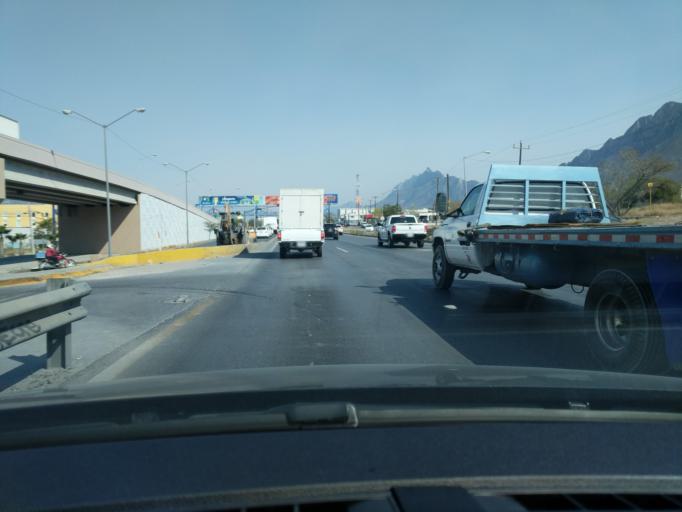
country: MX
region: Nuevo Leon
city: Santa Catarina
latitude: 25.6884
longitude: -100.4980
